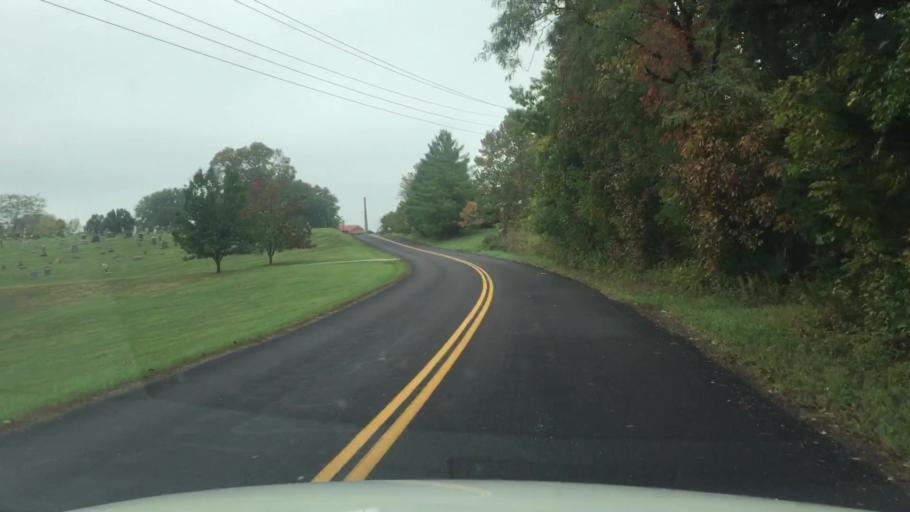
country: US
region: Missouri
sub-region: Boone County
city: Ashland
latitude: 38.8234
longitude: -92.3484
